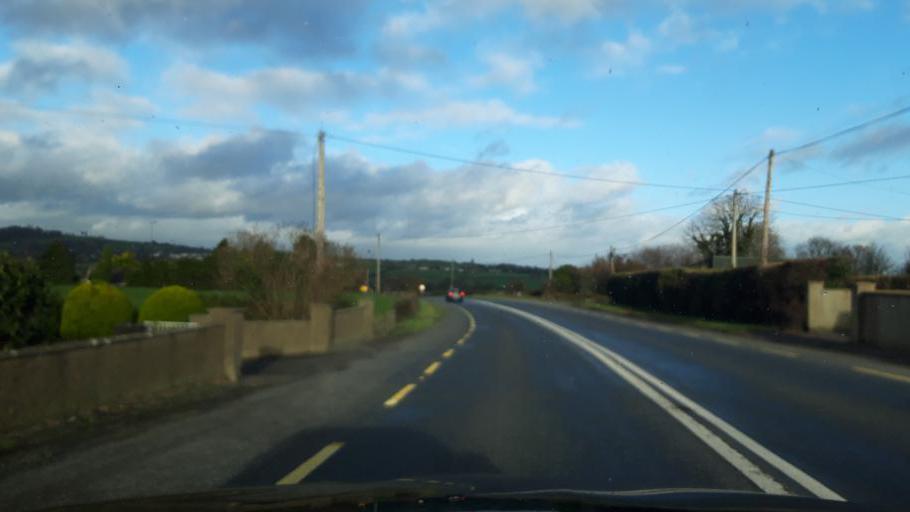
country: IE
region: Leinster
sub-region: An Mhi
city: Slane
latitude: 53.6931
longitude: -6.5394
